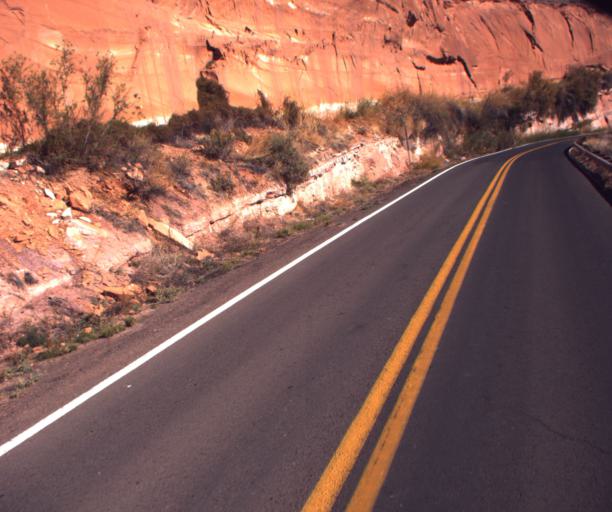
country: US
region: Arizona
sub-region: Coconino County
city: Tuba City
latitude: 36.1057
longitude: -111.2067
